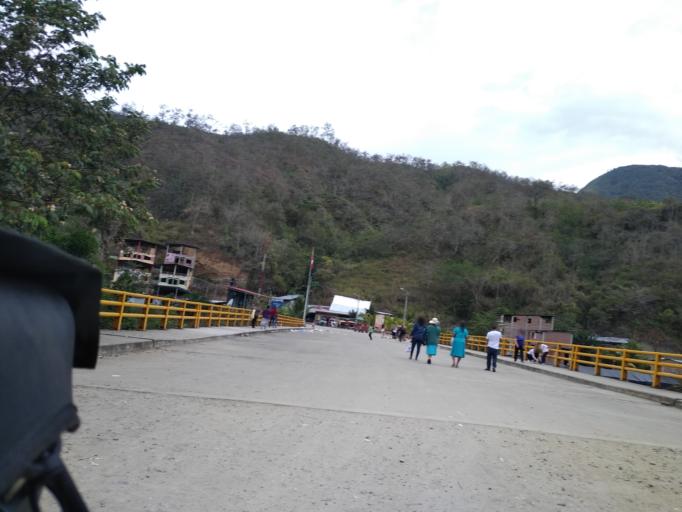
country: PE
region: Cajamarca
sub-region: Provincia de San Ignacio
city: Namballe
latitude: -4.9774
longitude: -79.1159
